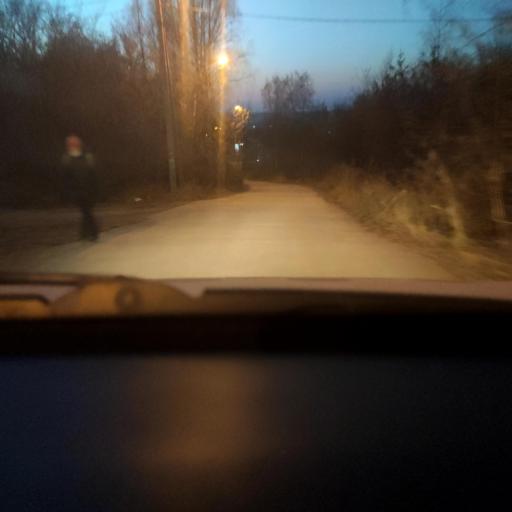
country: RU
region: Perm
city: Perm
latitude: 58.0570
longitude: 56.3398
